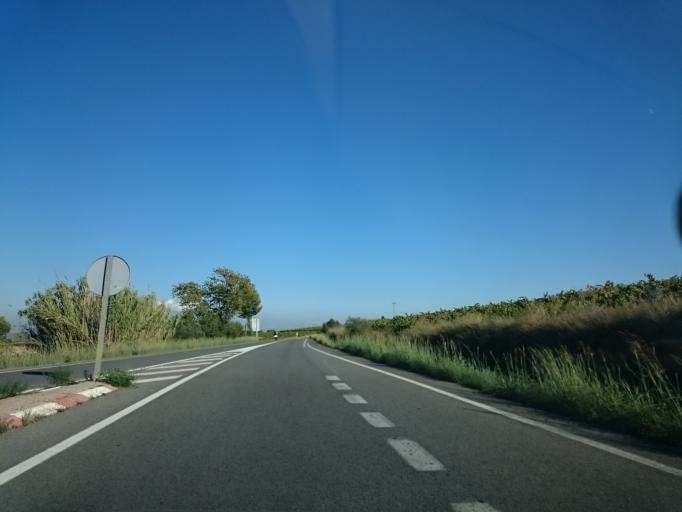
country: ES
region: Catalonia
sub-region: Provincia de Barcelona
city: Masquefa
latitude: 41.5024
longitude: 1.7896
